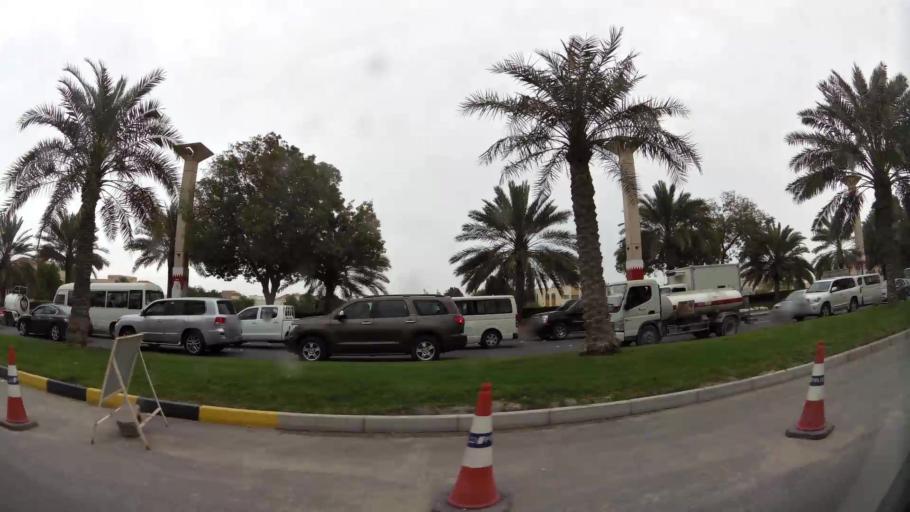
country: BH
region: Northern
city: Ar Rifa'
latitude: 26.1319
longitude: 50.5376
